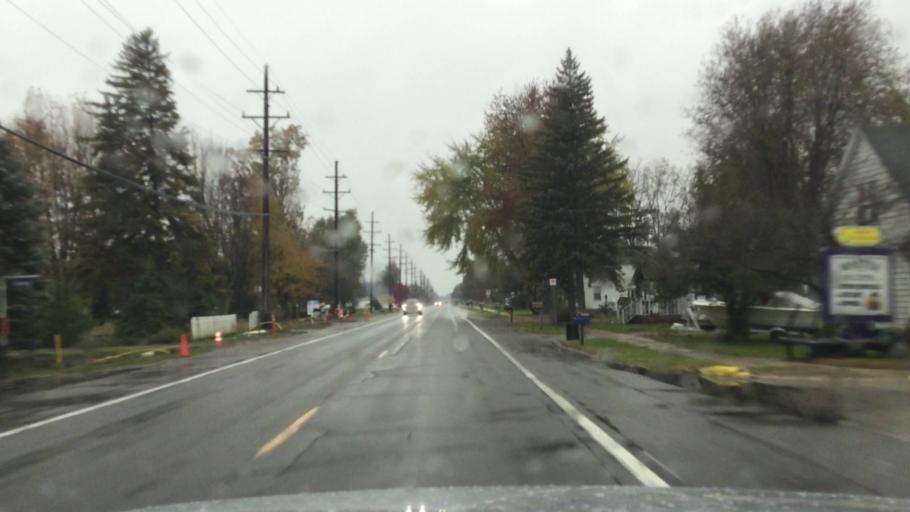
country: US
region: Michigan
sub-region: Saint Clair County
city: Pearl Beach
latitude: 42.6207
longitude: -82.5852
